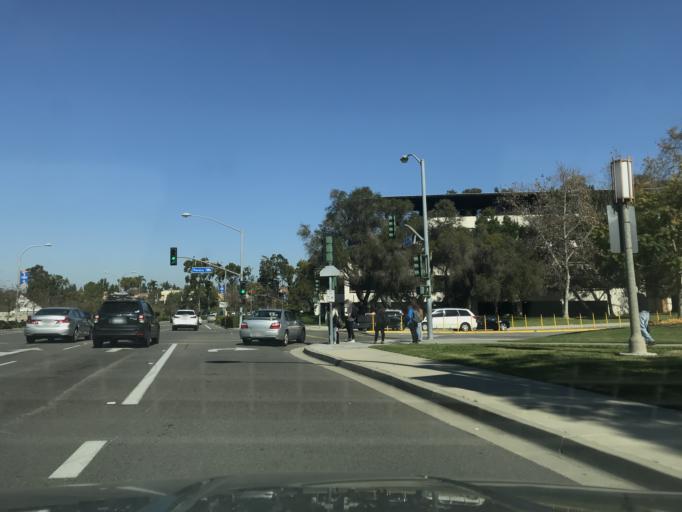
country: US
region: California
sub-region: Orange County
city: Irvine
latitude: 33.6497
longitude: -117.8431
